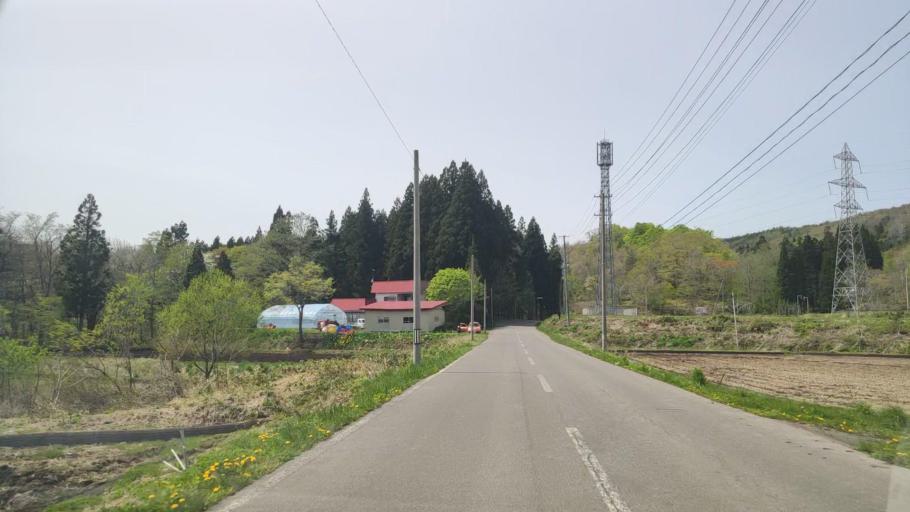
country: JP
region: Aomori
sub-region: Misawa Shi
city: Inuotose
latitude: 40.7898
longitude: 141.1014
